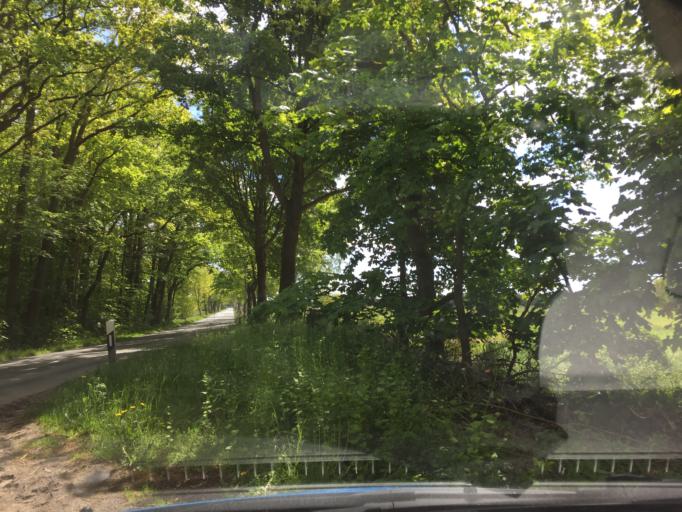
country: DE
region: Lower Saxony
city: Suderburg
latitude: 52.9245
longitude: 10.4965
